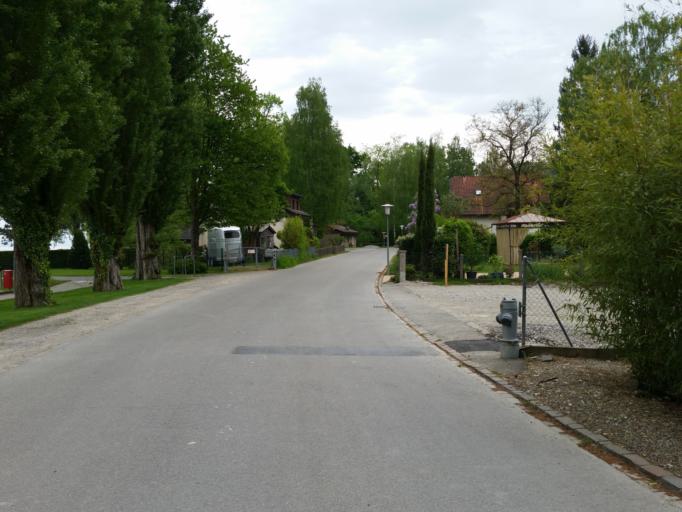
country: CH
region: Thurgau
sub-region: Kreuzlingen District
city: Guttingen
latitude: 47.6115
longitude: 9.2962
